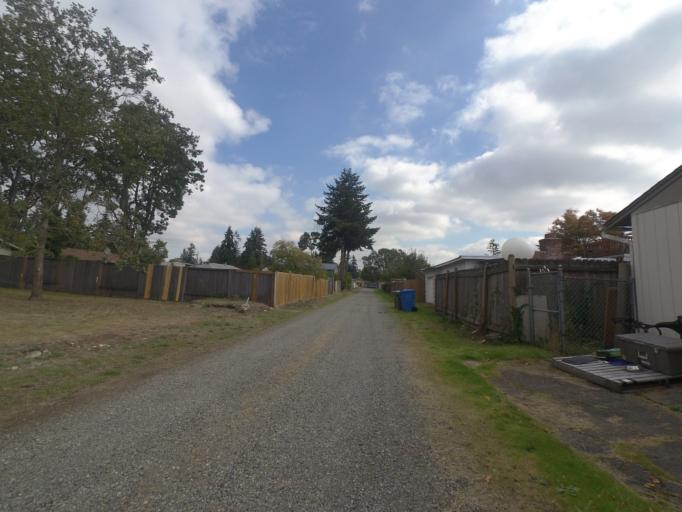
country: US
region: Washington
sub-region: Pierce County
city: Lakewood
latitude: 47.1737
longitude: -122.5253
